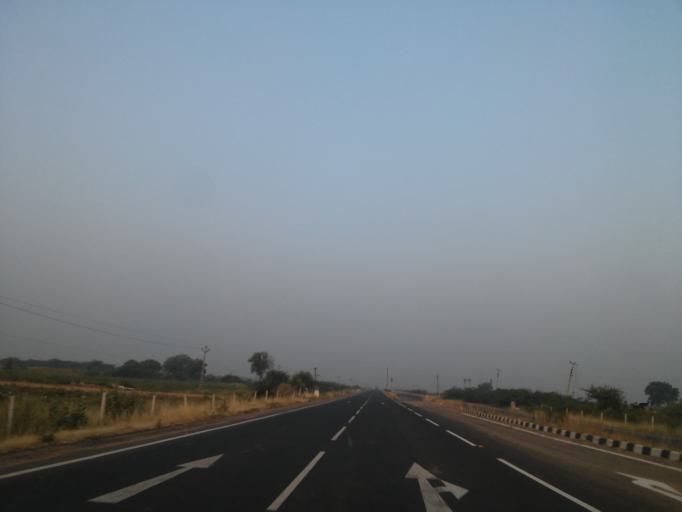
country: IN
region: Gujarat
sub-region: Rajkot
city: Morbi
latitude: 23.0631
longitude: 70.8398
